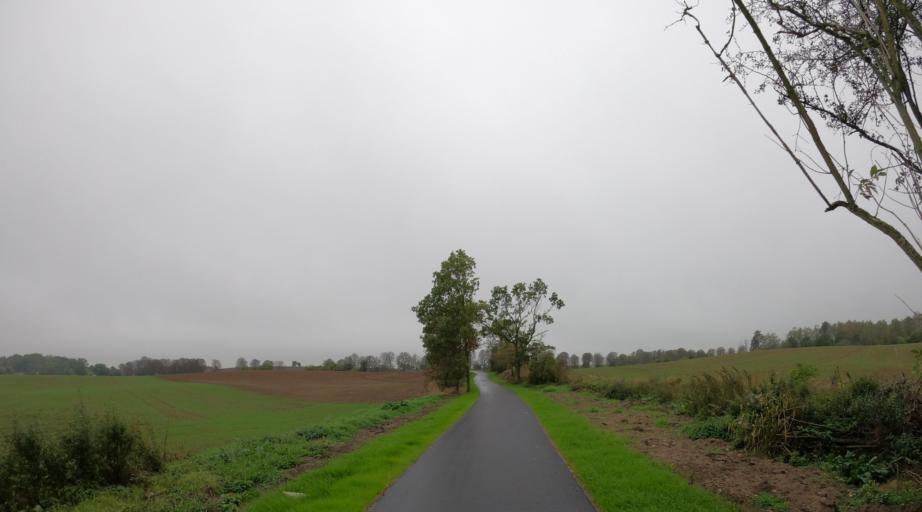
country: PL
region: West Pomeranian Voivodeship
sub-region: Powiat mysliborski
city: Mysliborz
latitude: 52.9074
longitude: 14.7476
